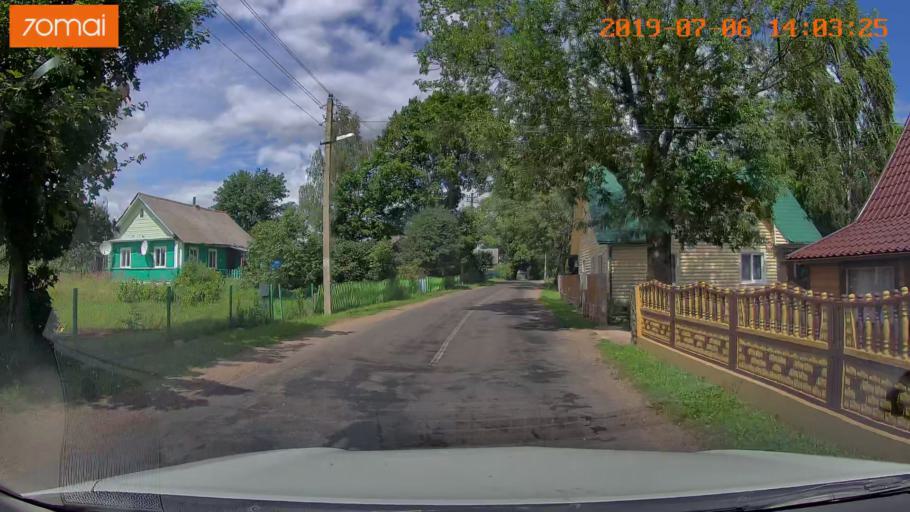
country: BY
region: Minsk
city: Ivyanyets
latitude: 53.8306
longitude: 26.8000
